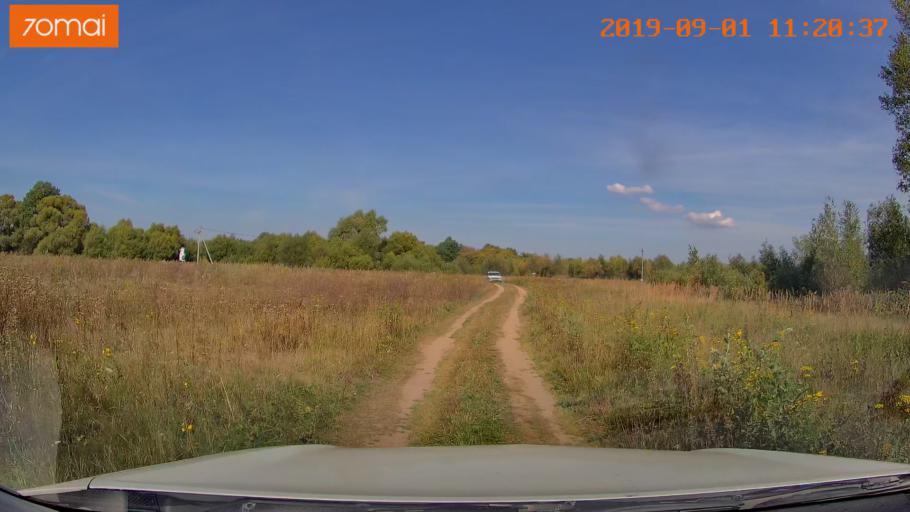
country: RU
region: Kaluga
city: Detchino
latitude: 54.8296
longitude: 36.3608
